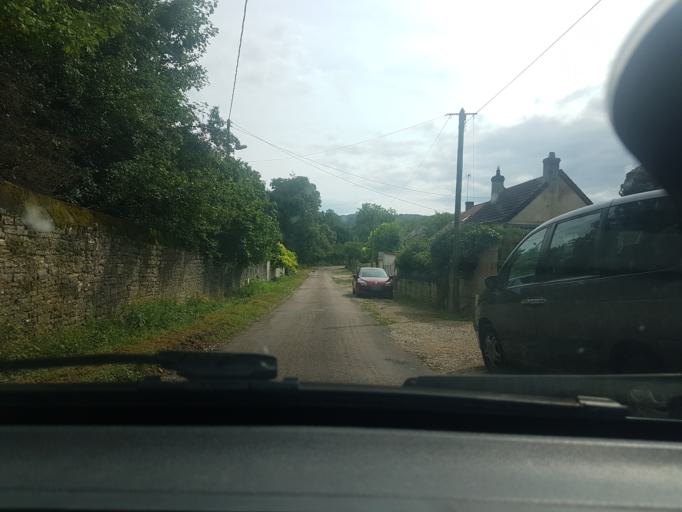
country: FR
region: Bourgogne
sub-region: Departement de Saone-et-Loire
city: Dracy-le-Fort
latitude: 46.8096
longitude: 4.7522
